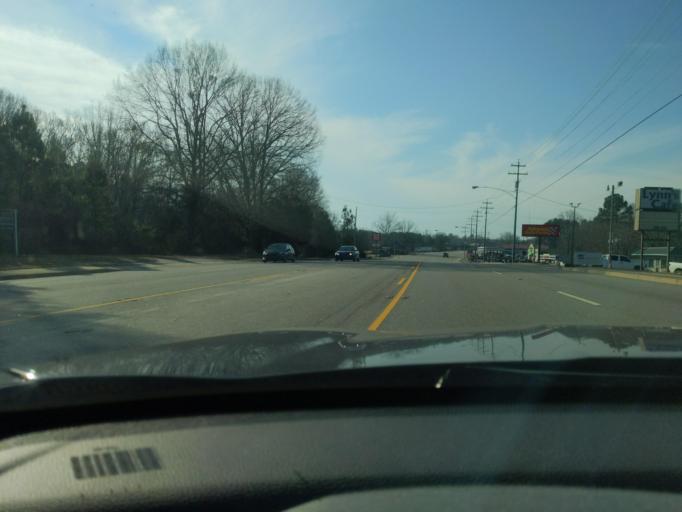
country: US
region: South Carolina
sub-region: Abbeville County
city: Abbeville
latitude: 34.1664
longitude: -82.3817
